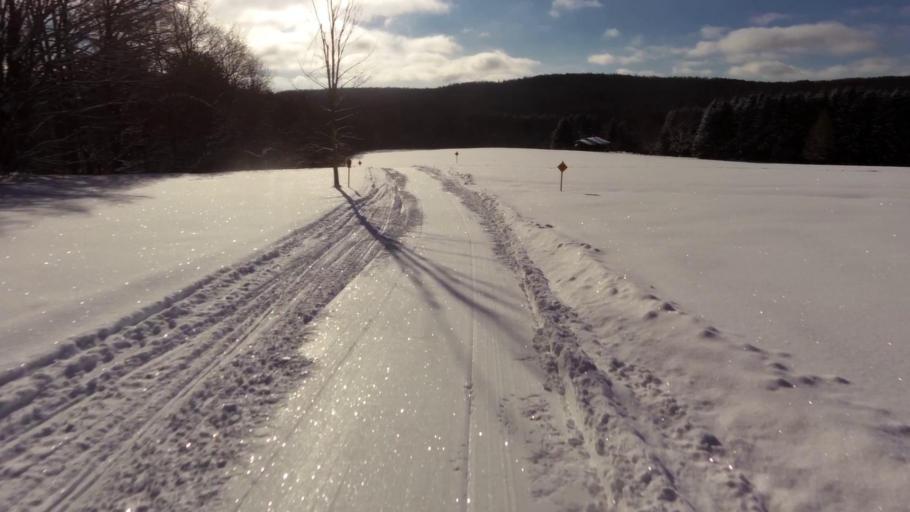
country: US
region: New York
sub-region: Chautauqua County
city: Falconer
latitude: 42.2561
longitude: -79.1705
